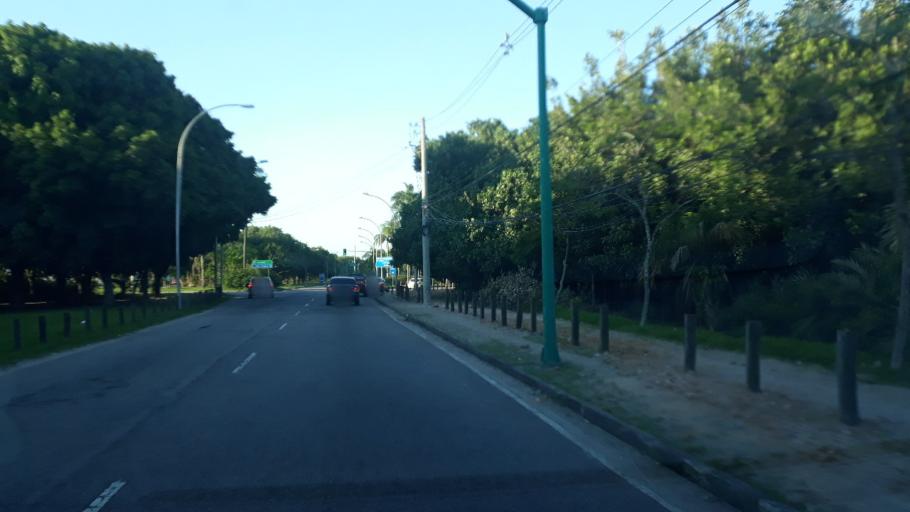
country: BR
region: Rio de Janeiro
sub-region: Rio De Janeiro
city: Rio de Janeiro
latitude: -22.9925
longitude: -43.3608
